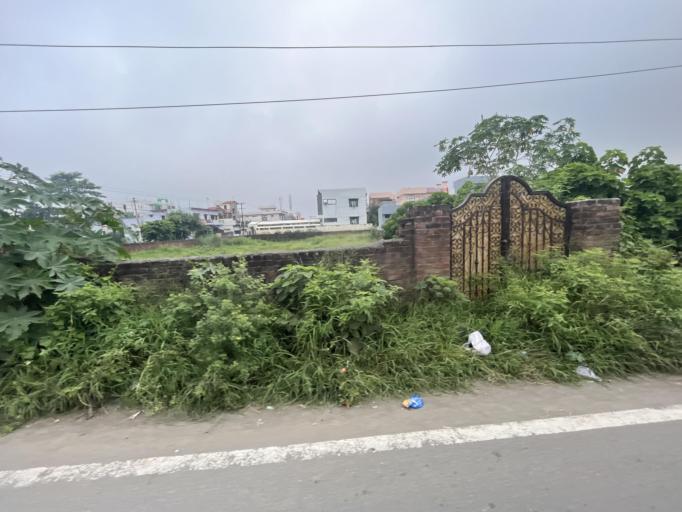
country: IN
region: Uttarakhand
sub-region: Naini Tal
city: Haldwani
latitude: 29.1943
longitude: 79.5047
